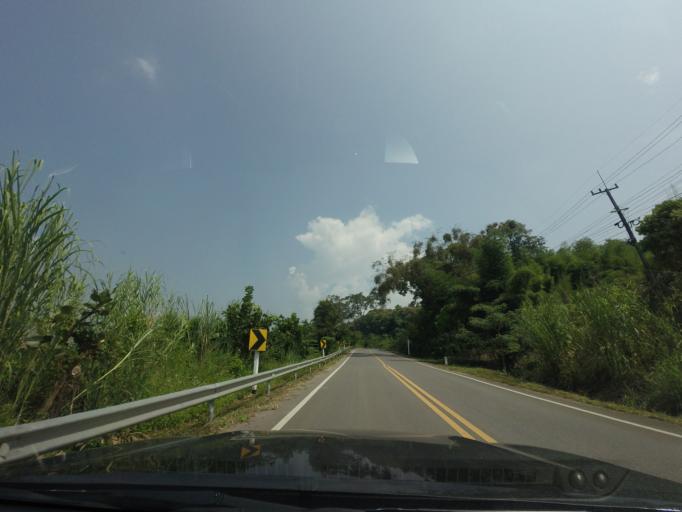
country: TH
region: Nan
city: Nan
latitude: 18.8745
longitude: 100.8338
